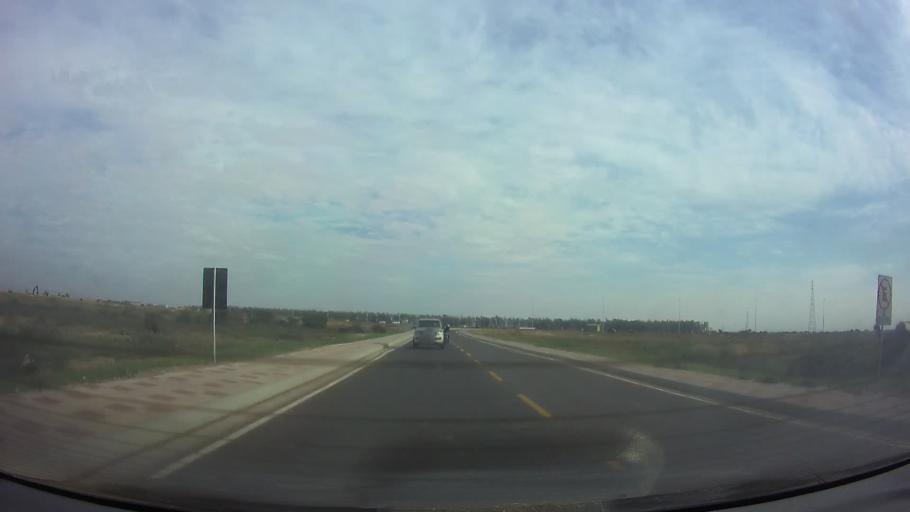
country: PY
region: Asuncion
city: Asuncion
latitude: -25.2481
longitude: -57.5932
